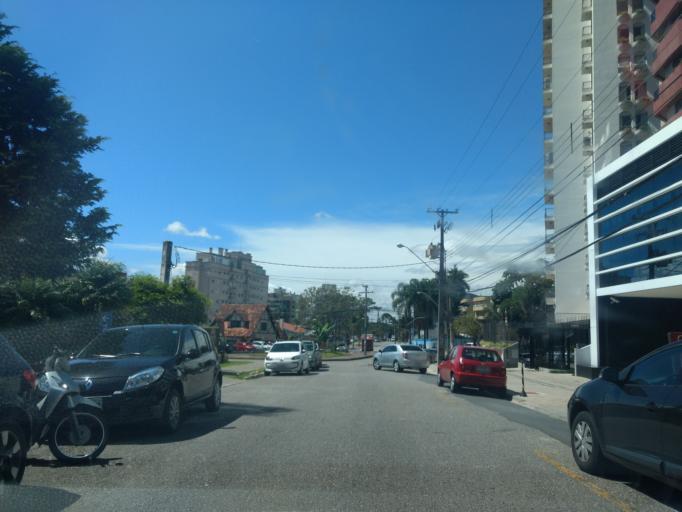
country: BR
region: Parana
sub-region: Curitiba
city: Curitiba
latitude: -25.4108
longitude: -49.2553
